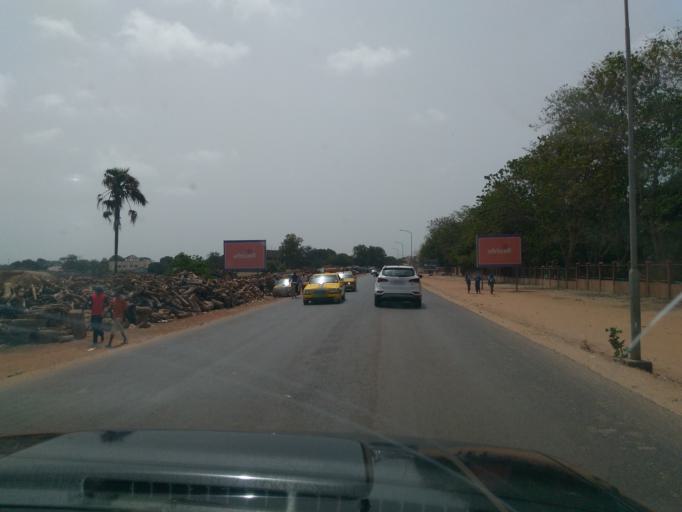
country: GM
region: Western
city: Sukuta
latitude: 13.4375
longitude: -16.6973
